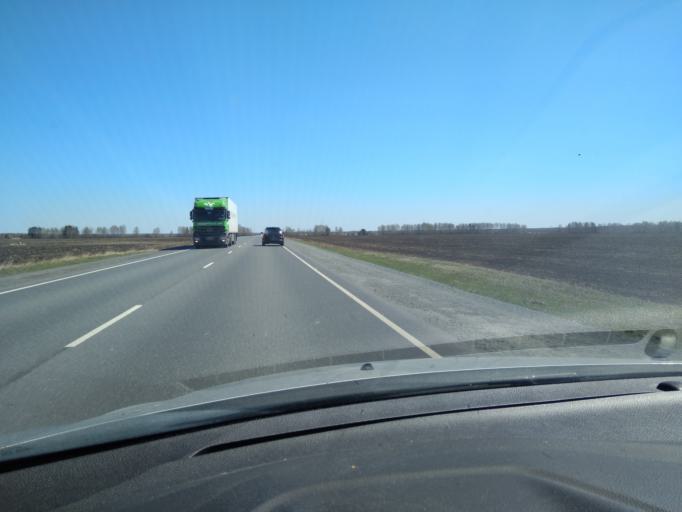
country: RU
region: Sverdlovsk
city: Tugulym
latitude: 57.0754
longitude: 64.7973
